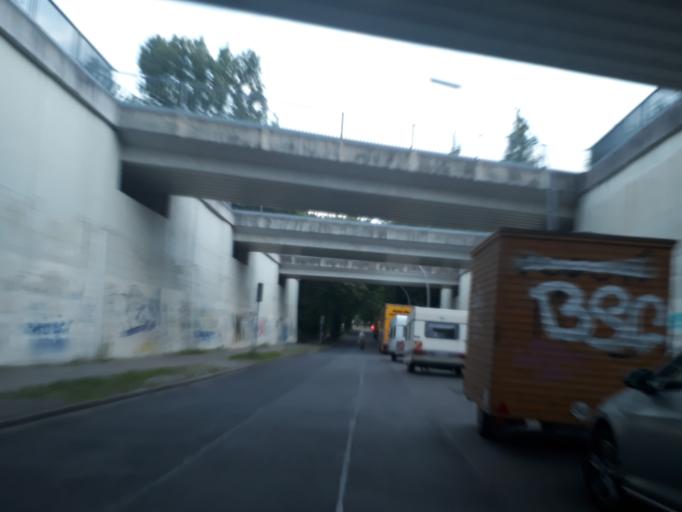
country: DE
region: Berlin
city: Westend
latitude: 52.5118
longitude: 13.2465
